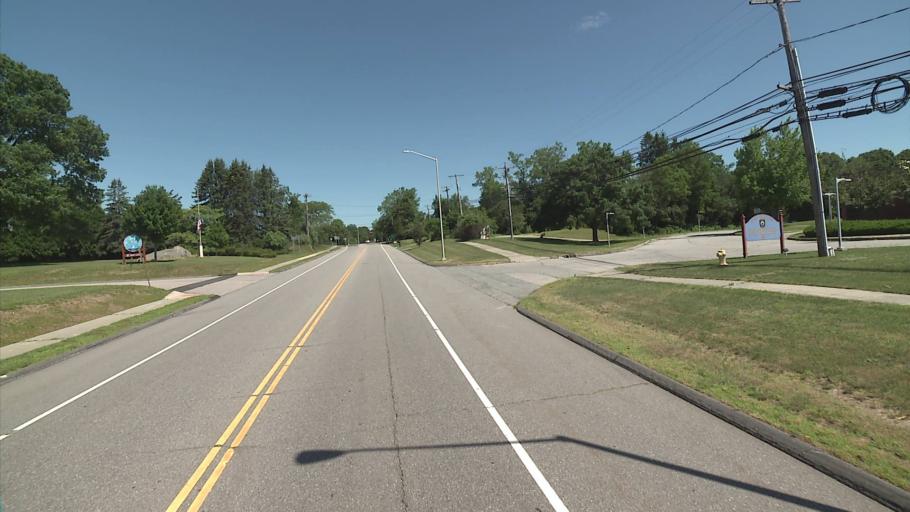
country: US
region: Connecticut
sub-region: New London County
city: Poquonock Bridge
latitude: 41.3433
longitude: -72.0108
